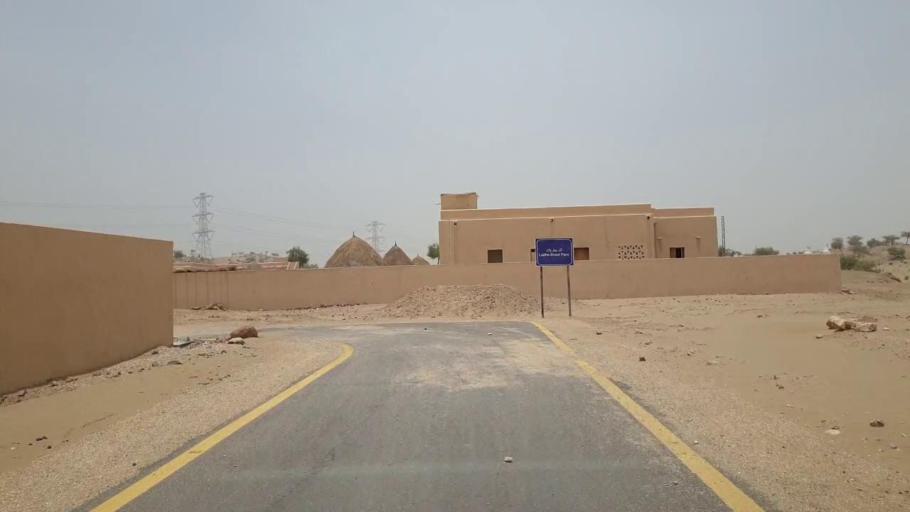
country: PK
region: Sindh
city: Islamkot
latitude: 24.7230
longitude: 70.3325
